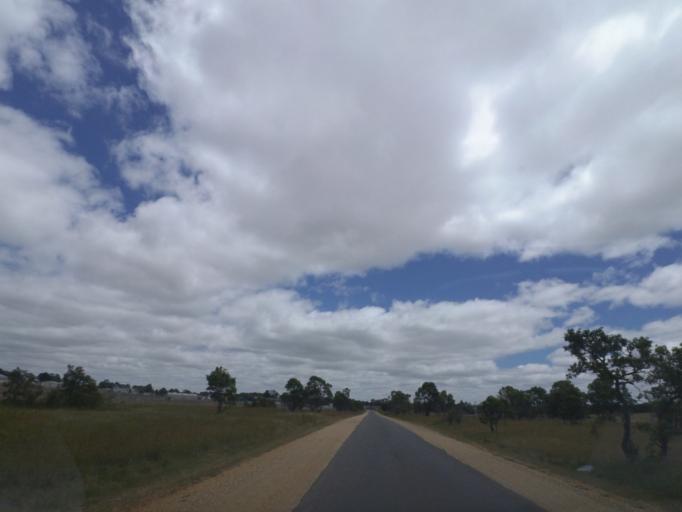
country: AU
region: Victoria
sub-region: Moorabool
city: Bacchus Marsh
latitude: -37.6123
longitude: 144.2443
